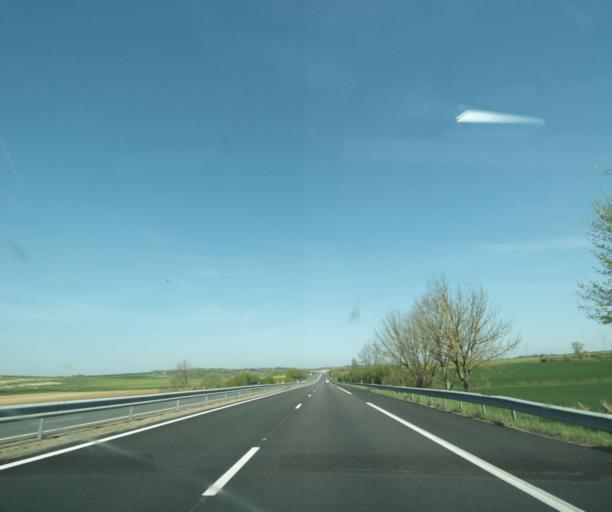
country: FR
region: Bourgogne
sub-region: Departement de la Nievre
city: La Charite-sur-Loire
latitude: 47.1410
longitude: 3.0443
